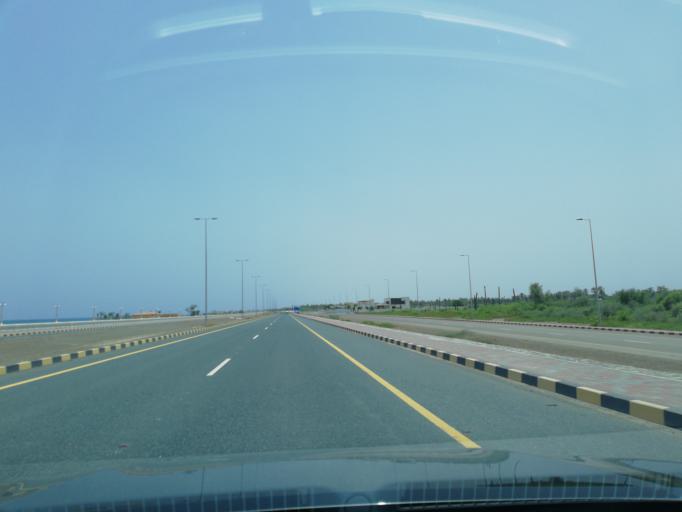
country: OM
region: Al Batinah
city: Shinas
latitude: 24.8188
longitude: 56.4410
